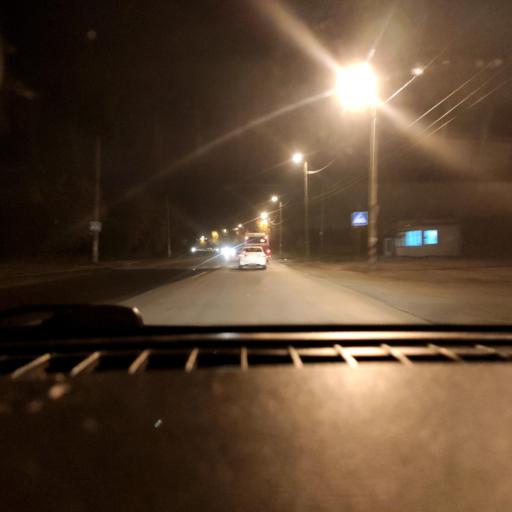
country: RU
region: Perm
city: Kondratovo
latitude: 57.9583
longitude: 56.1350
